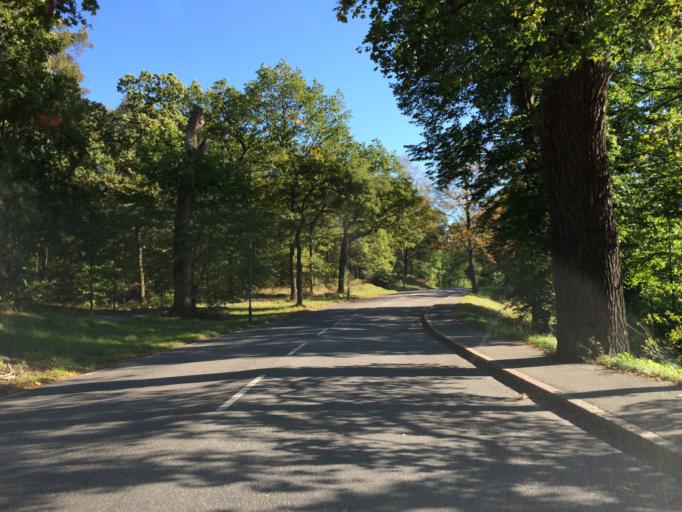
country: SE
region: Stockholm
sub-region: Nacka Kommun
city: Nacka
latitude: 59.3232
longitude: 18.1374
